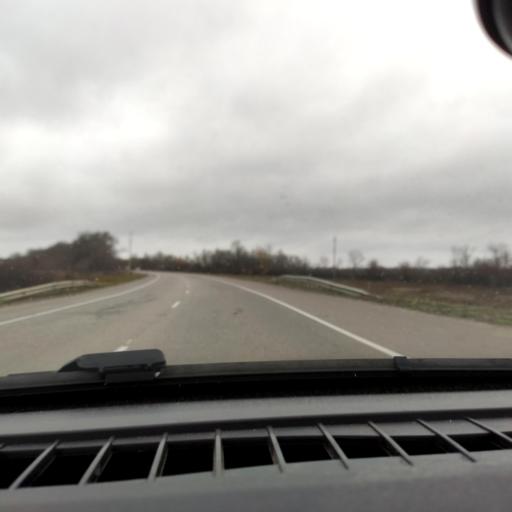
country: RU
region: Voronezj
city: Kolodeznyy
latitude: 51.3055
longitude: 39.0391
